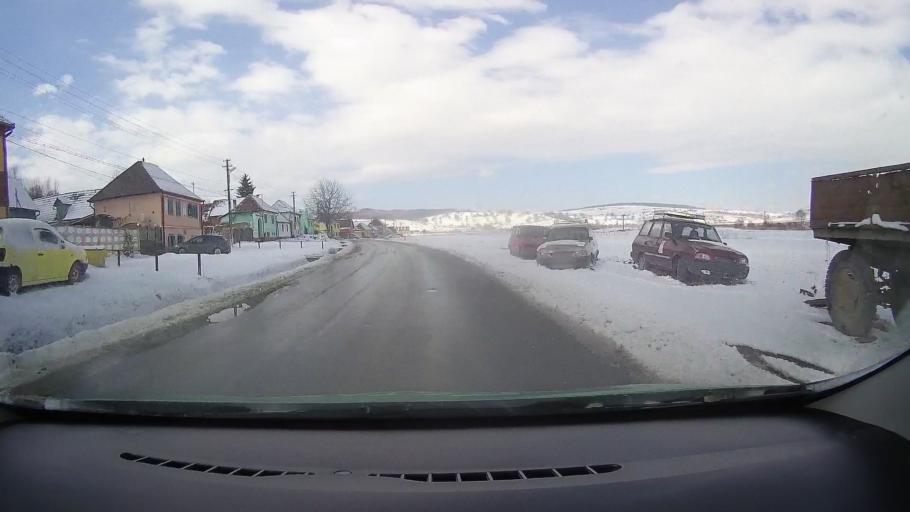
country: RO
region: Sibiu
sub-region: Comuna Altina
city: Altina
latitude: 45.9359
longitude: 24.4618
